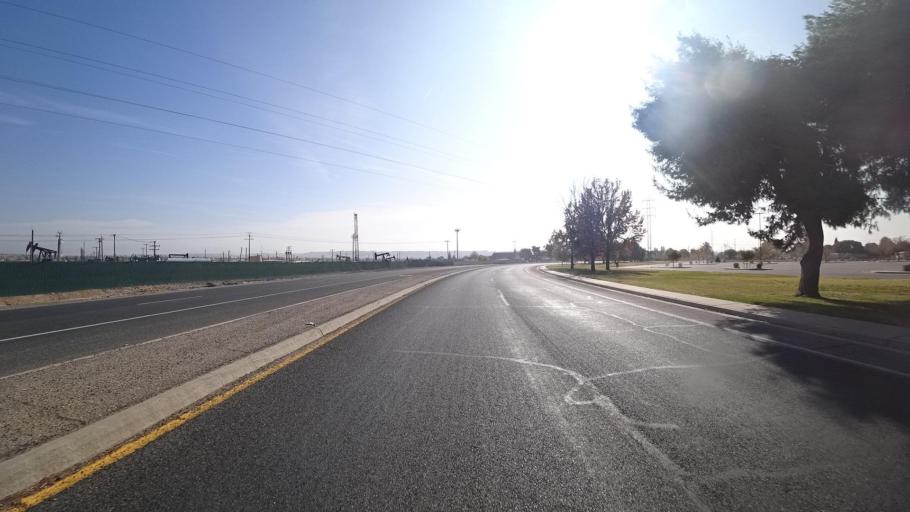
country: US
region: California
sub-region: Kern County
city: Oildale
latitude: 35.4379
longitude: -119.0137
